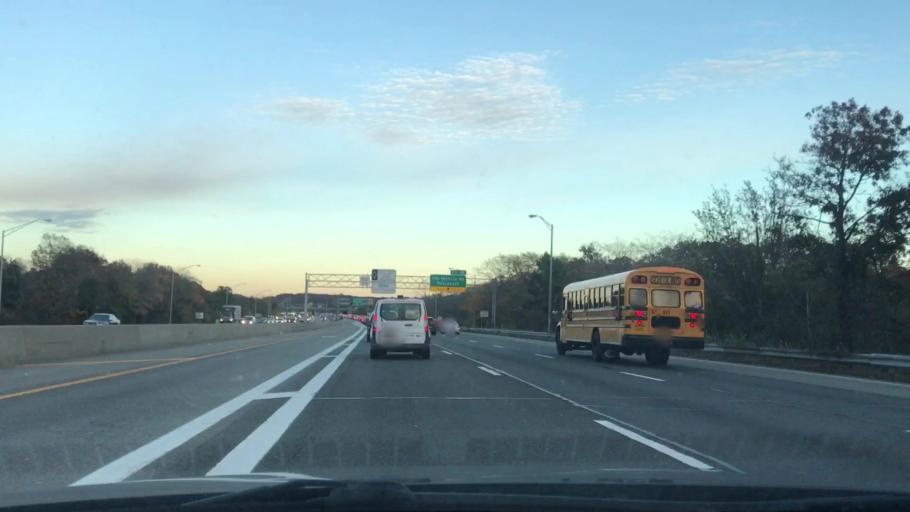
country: US
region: New York
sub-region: Suffolk County
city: Islandia
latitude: 40.8086
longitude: -73.1695
